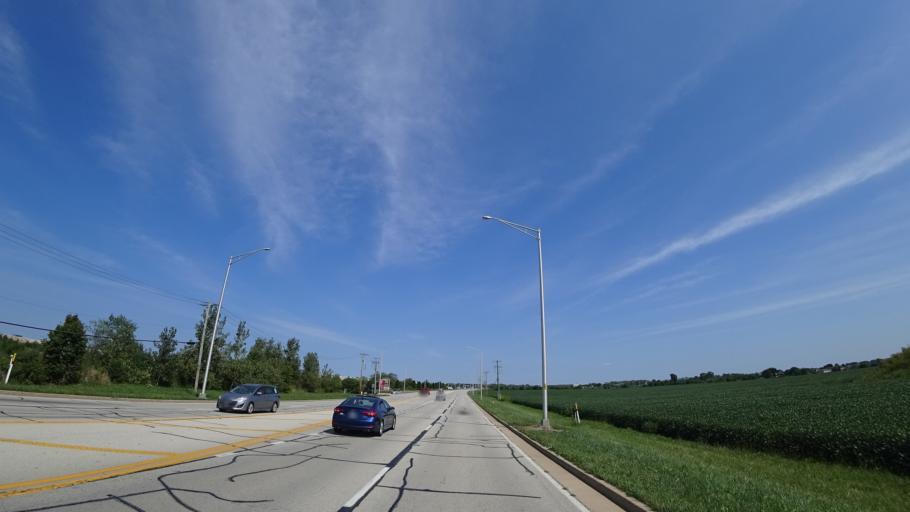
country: US
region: Illinois
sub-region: Will County
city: Frankfort Square
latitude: 41.5438
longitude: -87.8013
